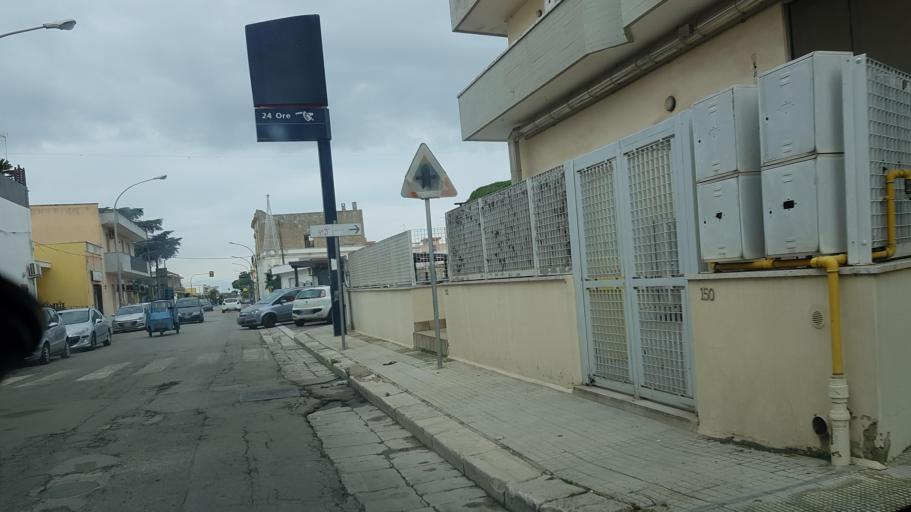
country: IT
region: Apulia
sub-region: Provincia di Lecce
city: Squinzano
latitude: 40.4390
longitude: 18.0376
